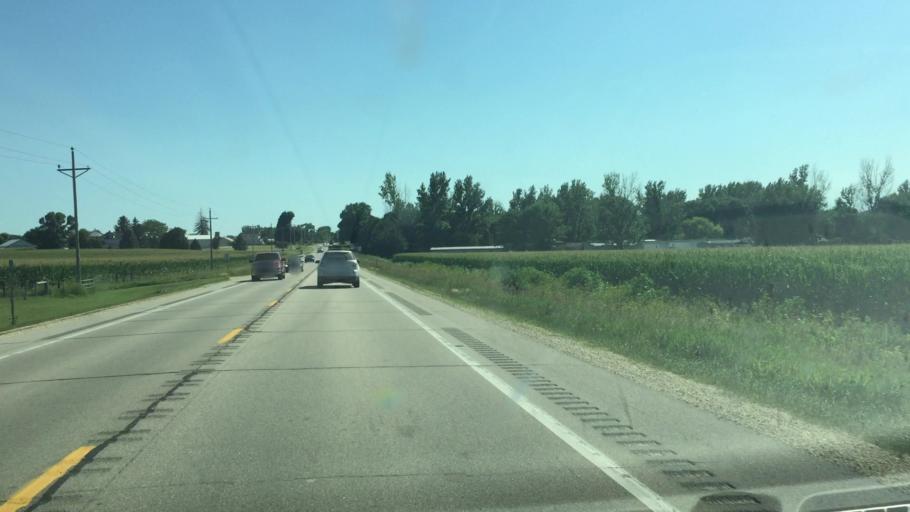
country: US
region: Iowa
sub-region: Linn County
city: Mount Vernon
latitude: 41.9356
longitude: -91.4049
